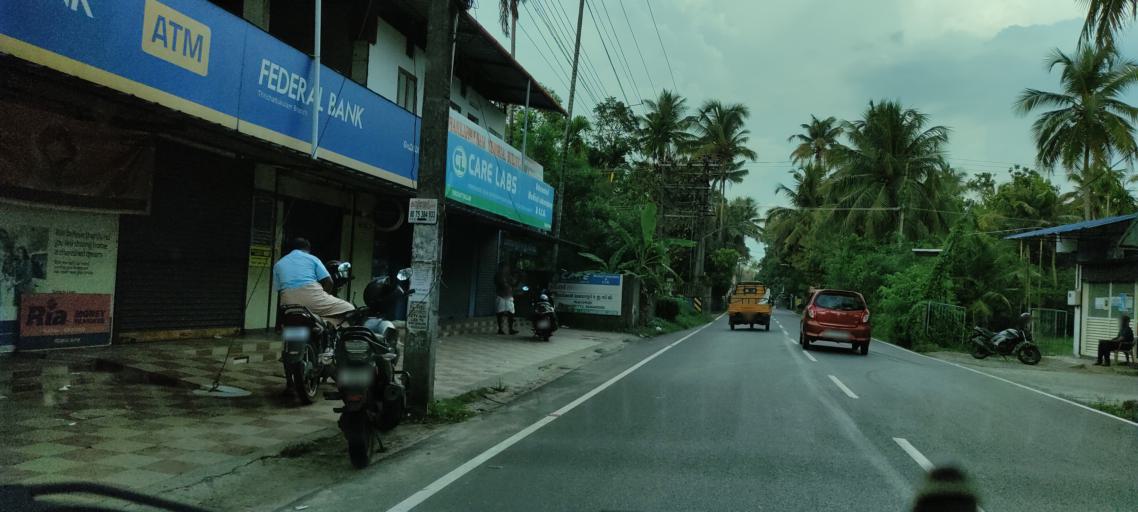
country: IN
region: Kerala
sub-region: Alappuzha
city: Kutiatodu
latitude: 9.8340
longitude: 76.3356
